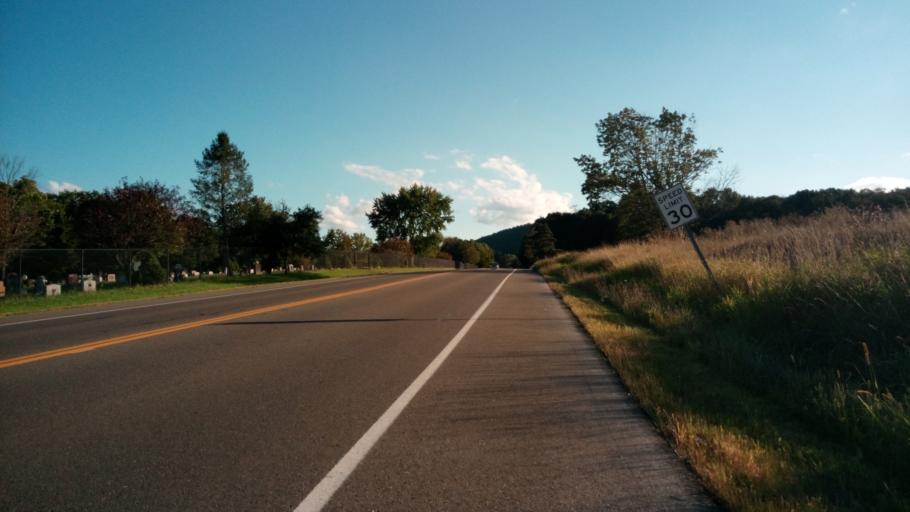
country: US
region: New York
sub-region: Chemung County
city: Elmira Heights
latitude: 42.1111
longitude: -76.8300
